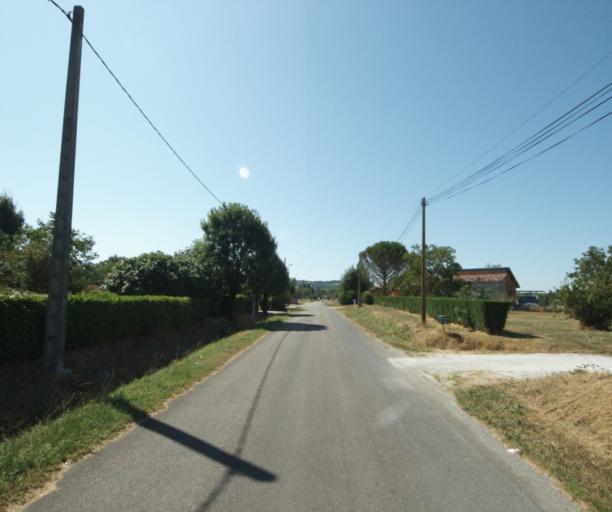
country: FR
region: Midi-Pyrenees
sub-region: Departement de la Haute-Garonne
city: Revel
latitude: 43.4691
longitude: 1.9983
